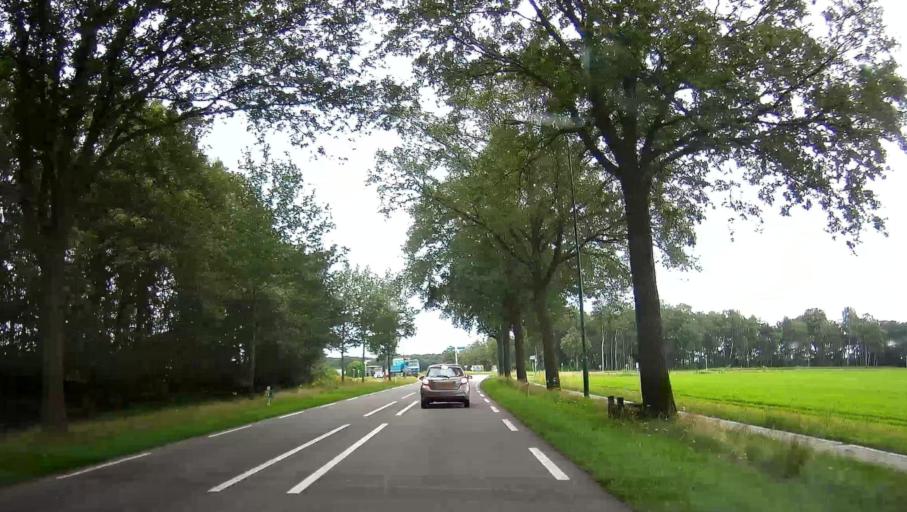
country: NL
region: North Brabant
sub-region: Gemeente Bladel en Netersel
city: Bladel
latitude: 51.3880
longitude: 5.1555
